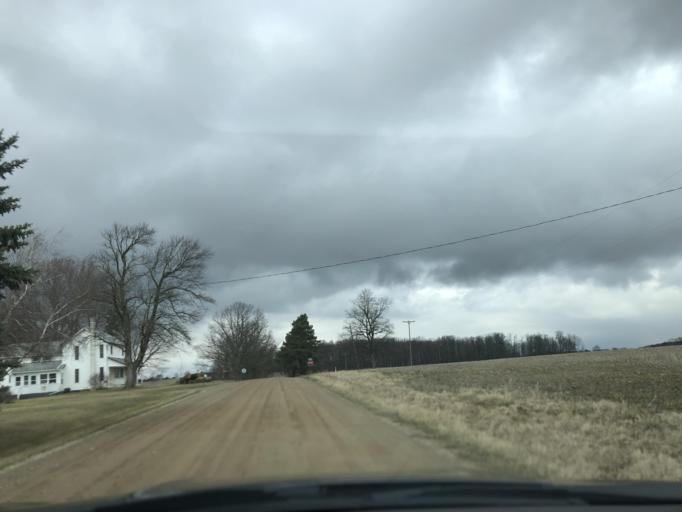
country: US
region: Michigan
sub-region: Clinton County
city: Saint Johns
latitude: 43.0961
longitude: -84.6106
